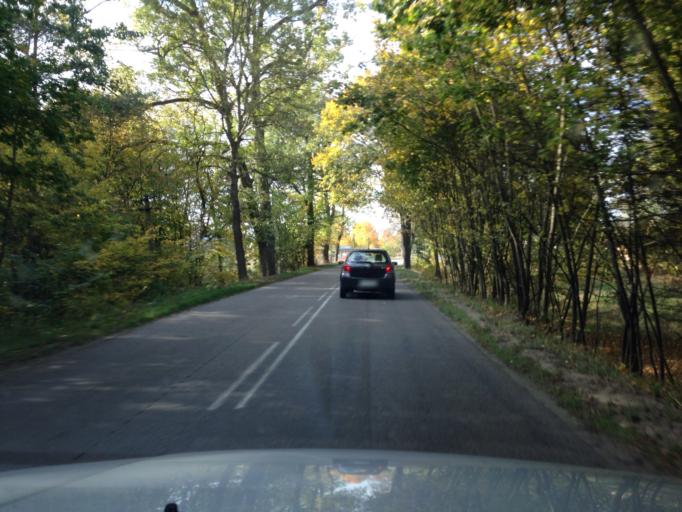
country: PL
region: Pomeranian Voivodeship
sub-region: Powiat koscierski
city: Stara Kiszewa
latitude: 53.9837
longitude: 18.2002
